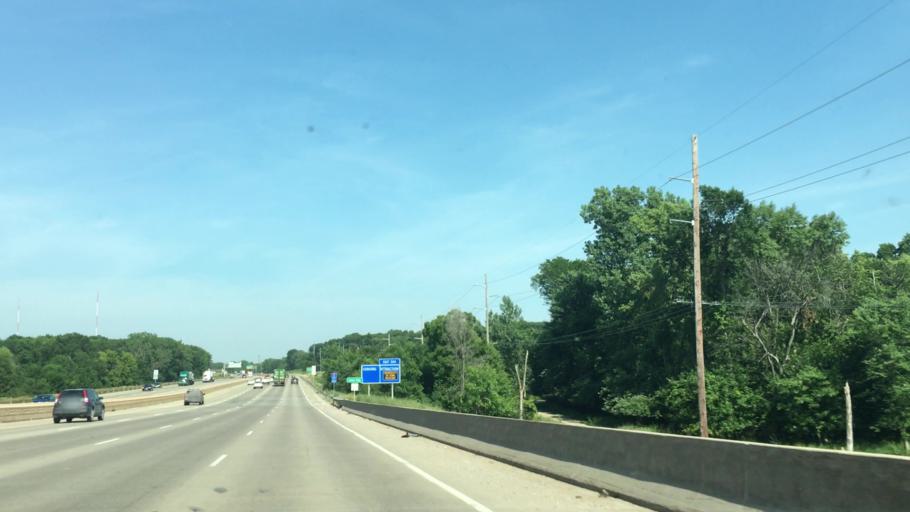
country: US
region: Iowa
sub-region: Johnson County
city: Coralville
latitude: 41.6851
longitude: -91.5571
